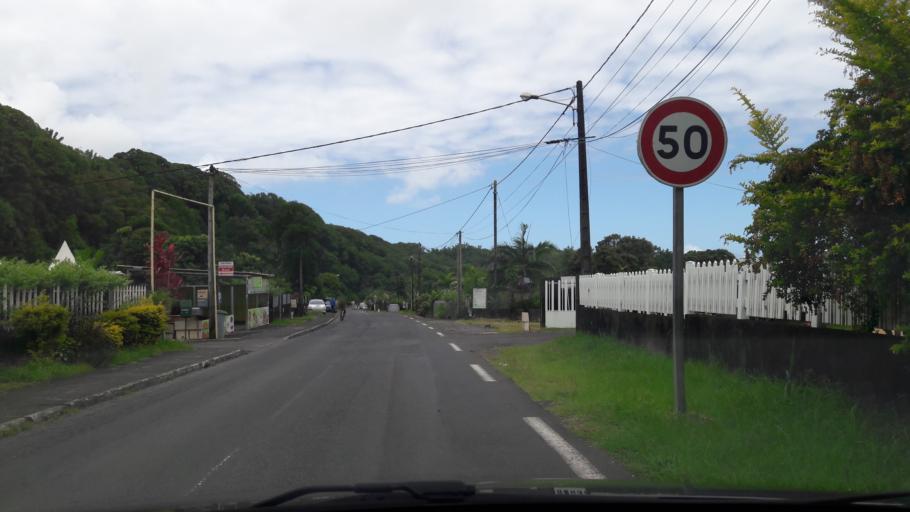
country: RE
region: Reunion
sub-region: Reunion
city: Saint-Andre
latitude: -20.9816
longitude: 55.6305
